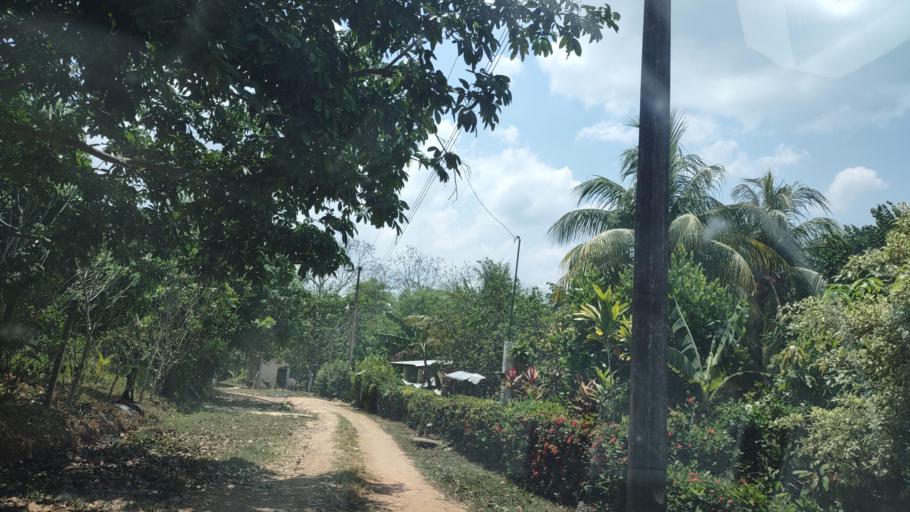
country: MX
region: Veracruz
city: Las Choapas
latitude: 17.9288
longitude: -94.1496
